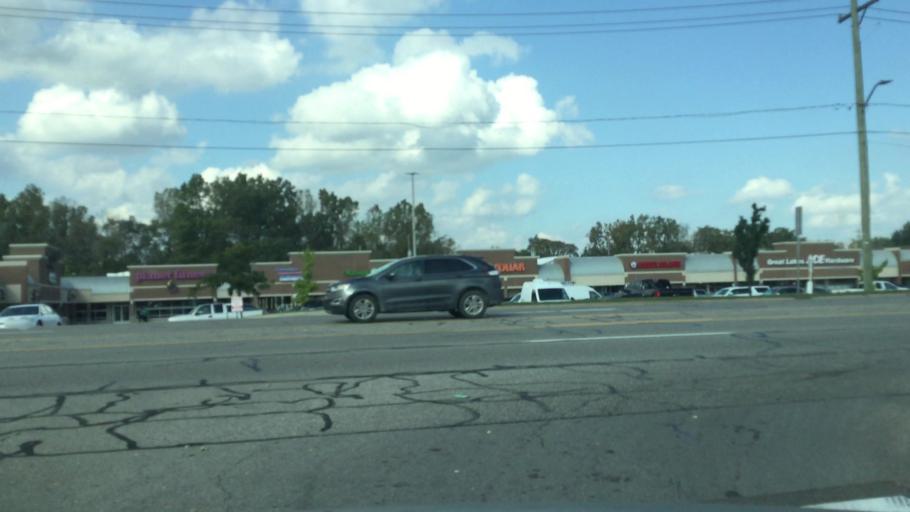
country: US
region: Michigan
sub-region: Oakland County
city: Waterford
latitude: 42.6601
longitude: -83.3889
